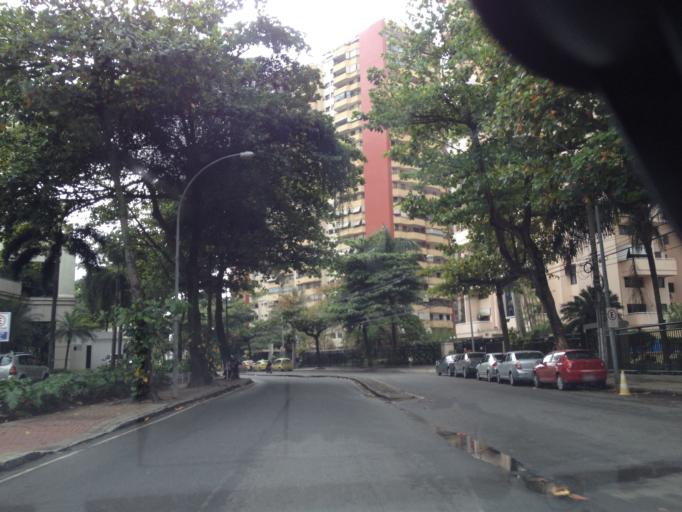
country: BR
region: Rio de Janeiro
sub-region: Rio De Janeiro
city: Rio de Janeiro
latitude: -23.0054
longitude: -43.3268
